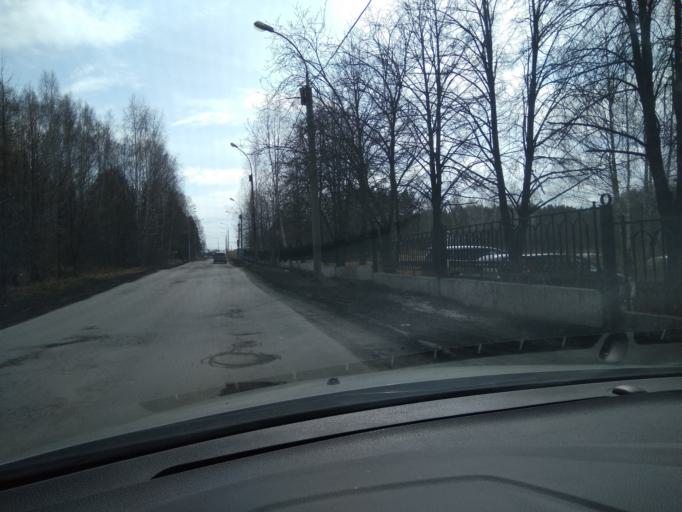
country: RU
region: Sverdlovsk
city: Shuvakish
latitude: 56.8948
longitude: 60.4853
